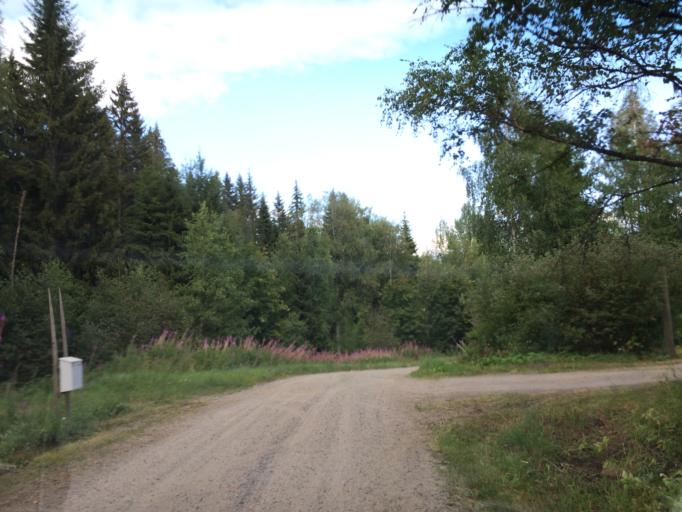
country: FI
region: Haeme
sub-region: Haemeenlinna
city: Hauho
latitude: 61.0781
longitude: 24.6460
